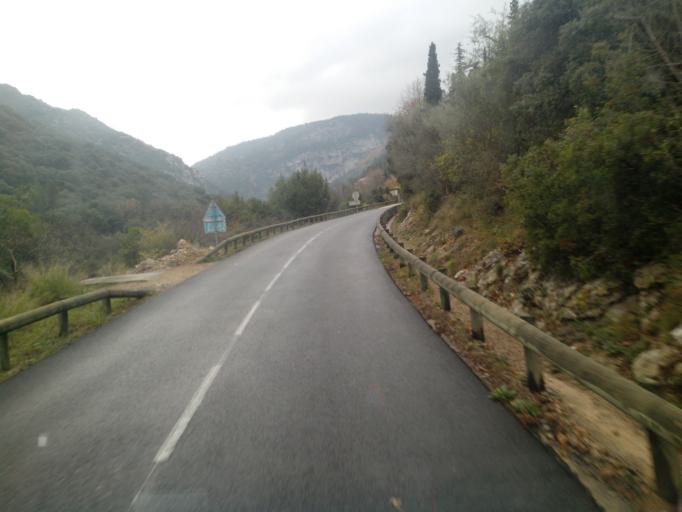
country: FR
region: Languedoc-Roussillon
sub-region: Departement de l'Herault
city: Saint-Jean-de-Fos
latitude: 43.7365
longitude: 3.5564
